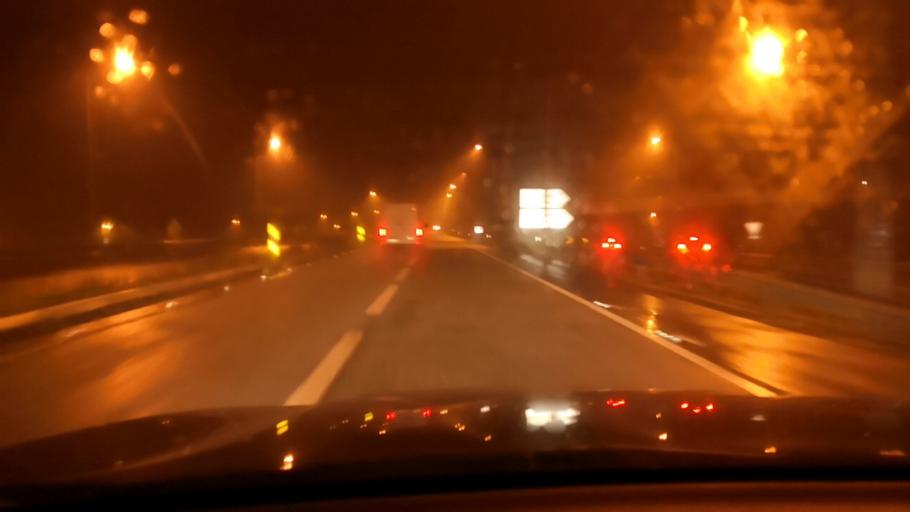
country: PT
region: Viseu
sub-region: Santa Comba Dao
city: Santa Comba Dao
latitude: 40.4388
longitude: -8.1095
